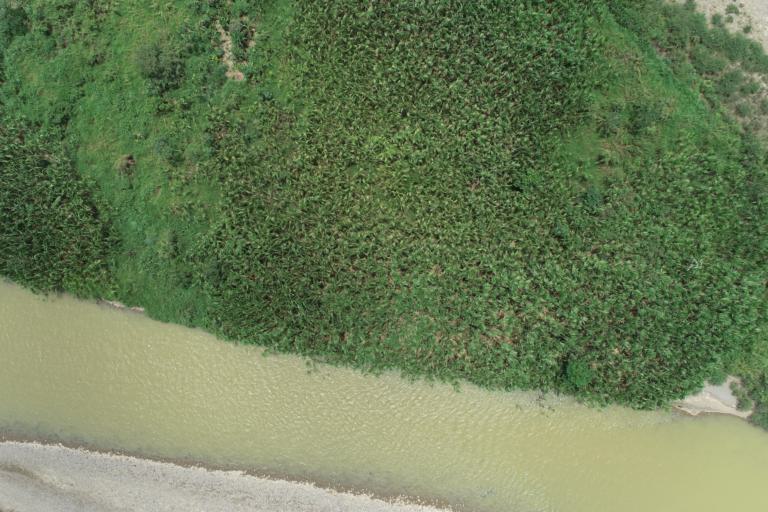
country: BO
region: La Paz
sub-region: Provincia Larecaja
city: Guanay
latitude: -15.7692
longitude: -67.6680
